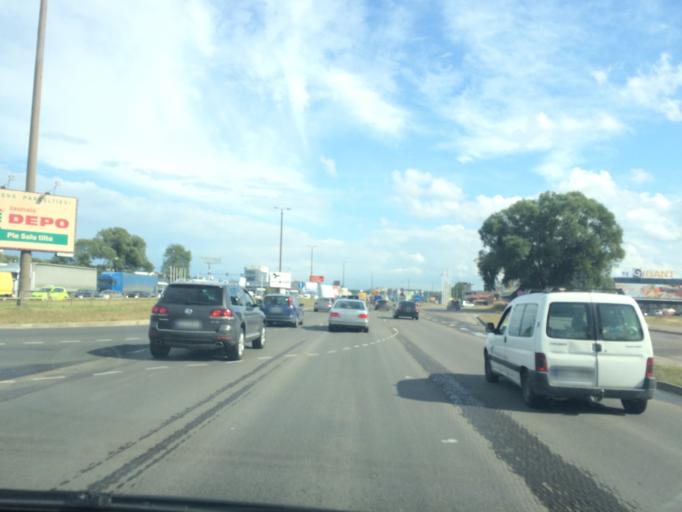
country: LV
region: Riga
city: Riga
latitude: 56.9331
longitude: 24.1444
